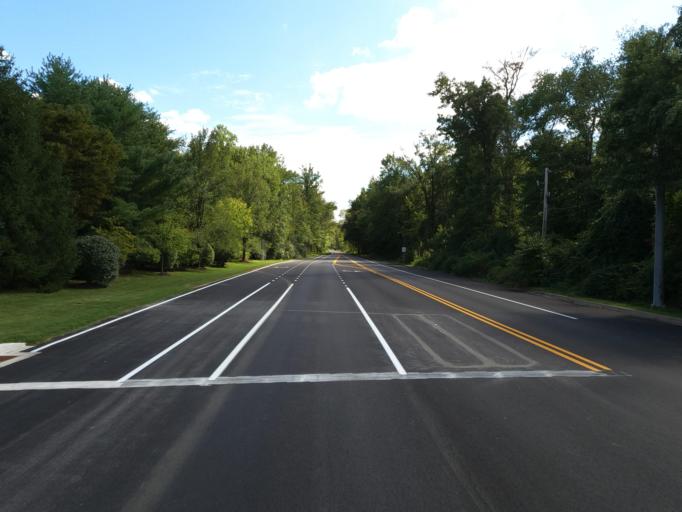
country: US
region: Delaware
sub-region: New Castle County
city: Glasgow
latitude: 39.6018
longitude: -75.7741
